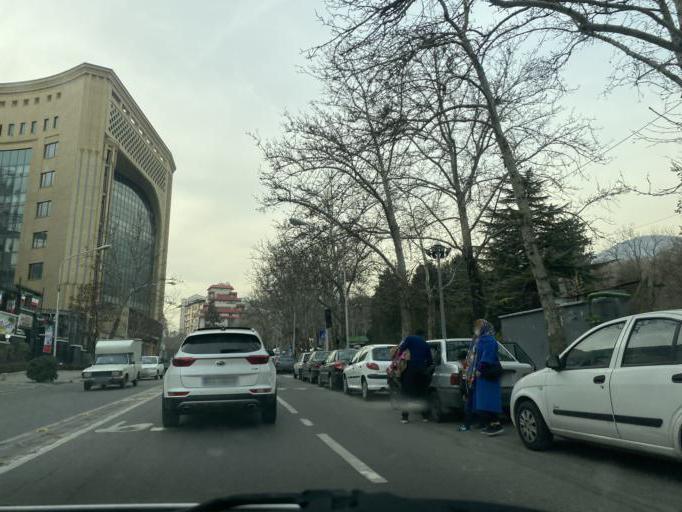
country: IR
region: Tehran
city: Tajrish
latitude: 35.8069
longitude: 51.4715
